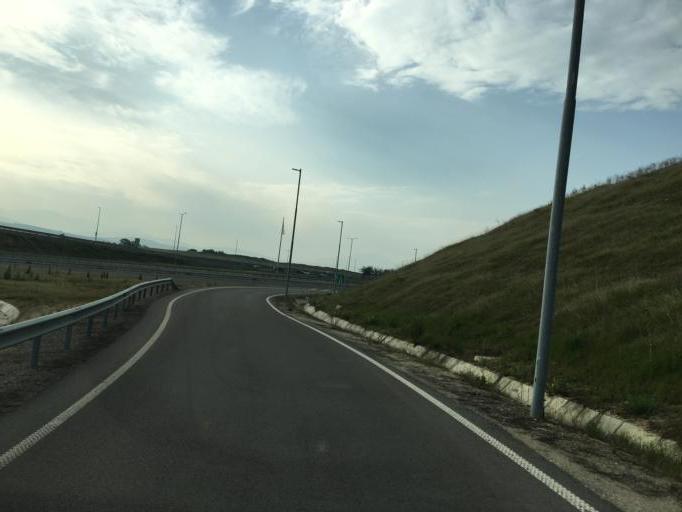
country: BG
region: Kyustendil
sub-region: Obshtina Kocherinovo
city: Kocherinovo
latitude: 42.0542
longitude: 23.0469
